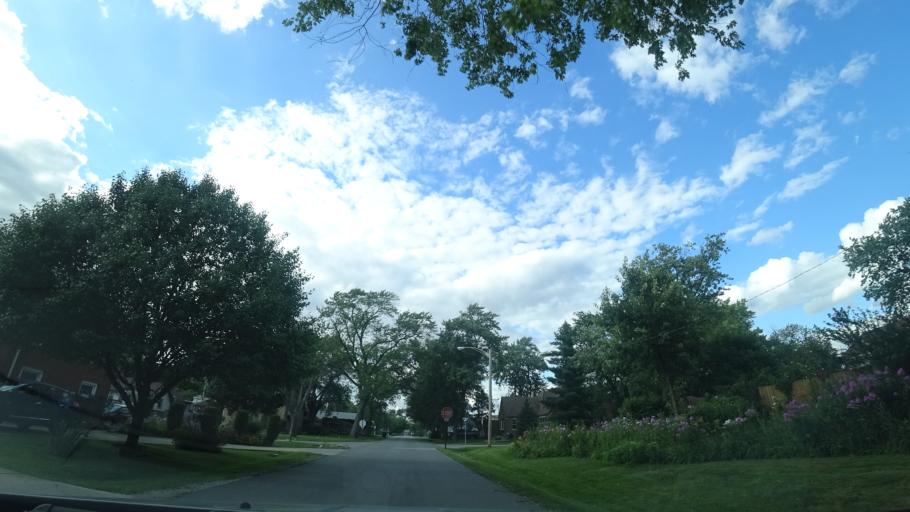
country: US
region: Illinois
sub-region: Cook County
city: Merrionette Park
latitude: 41.6809
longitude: -87.7126
